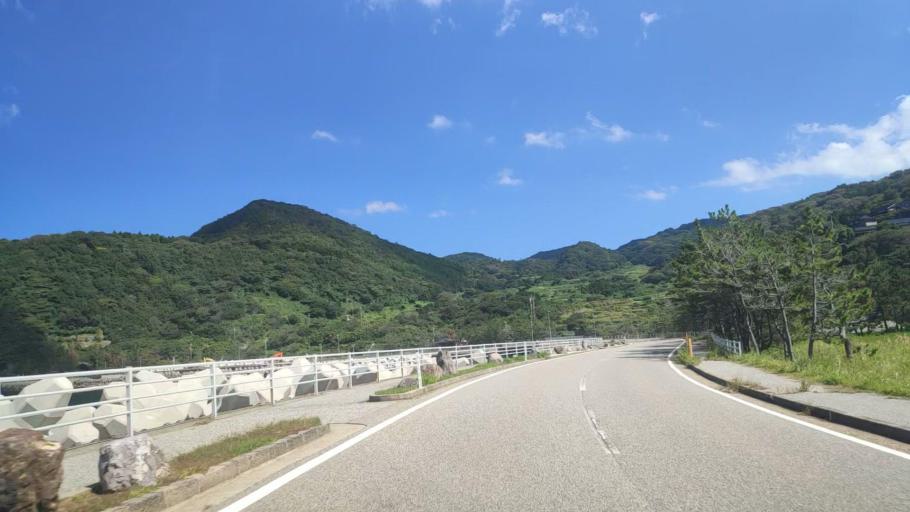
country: JP
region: Ishikawa
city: Nanao
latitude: 37.4715
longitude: 137.0902
